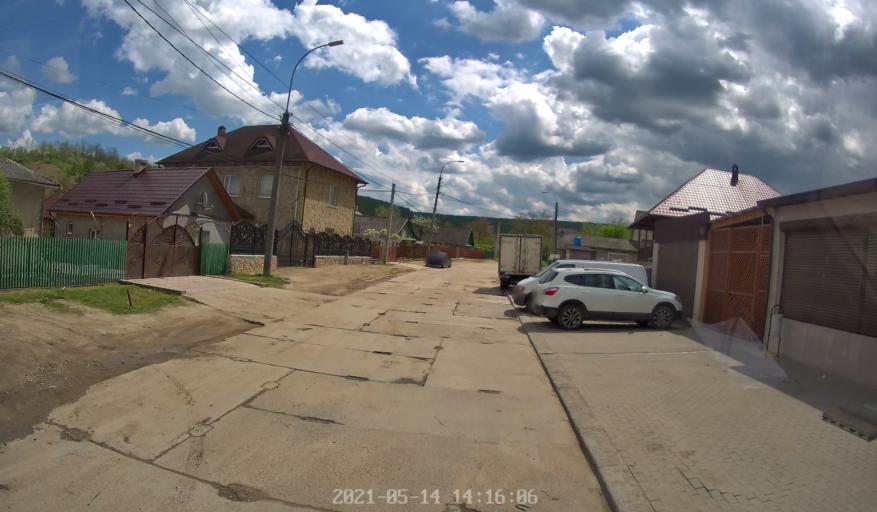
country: MD
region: Hincesti
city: Hincesti
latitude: 46.8239
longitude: 28.5853
